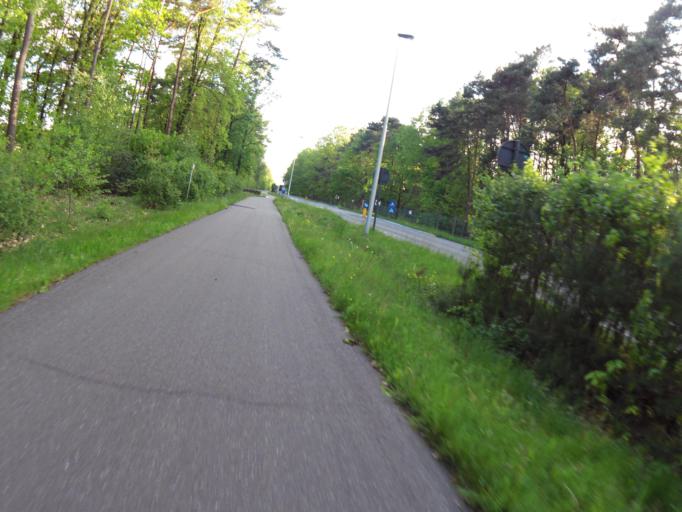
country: BE
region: Flanders
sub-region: Provincie Limburg
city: Zutendaal
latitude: 50.9455
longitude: 5.5980
